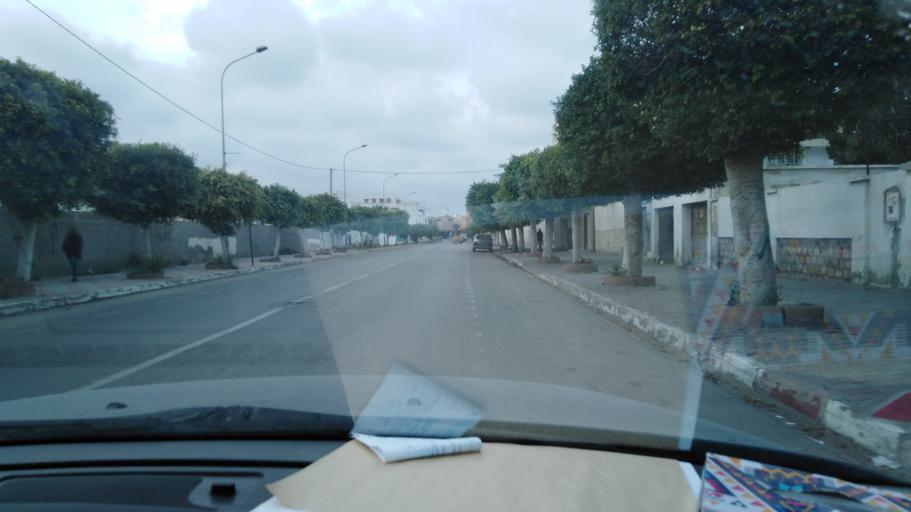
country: TN
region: Safaqis
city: Sfax
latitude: 34.7302
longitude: 10.7587
